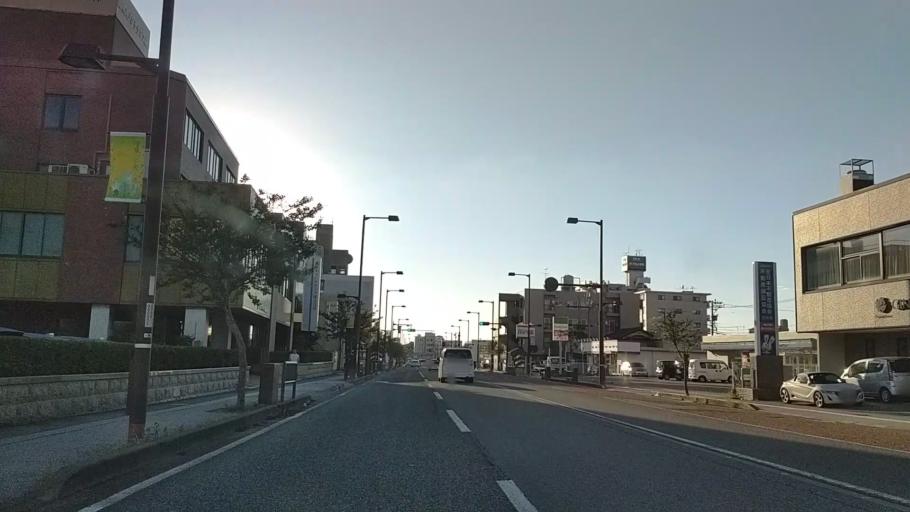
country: JP
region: Ishikawa
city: Nonoichi
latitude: 36.5584
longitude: 136.6429
